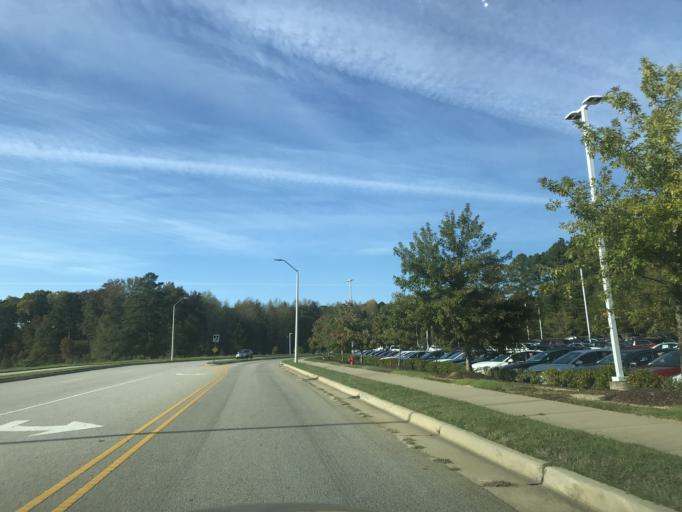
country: US
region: North Carolina
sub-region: Wake County
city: Wake Forest
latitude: 35.8912
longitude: -78.5652
